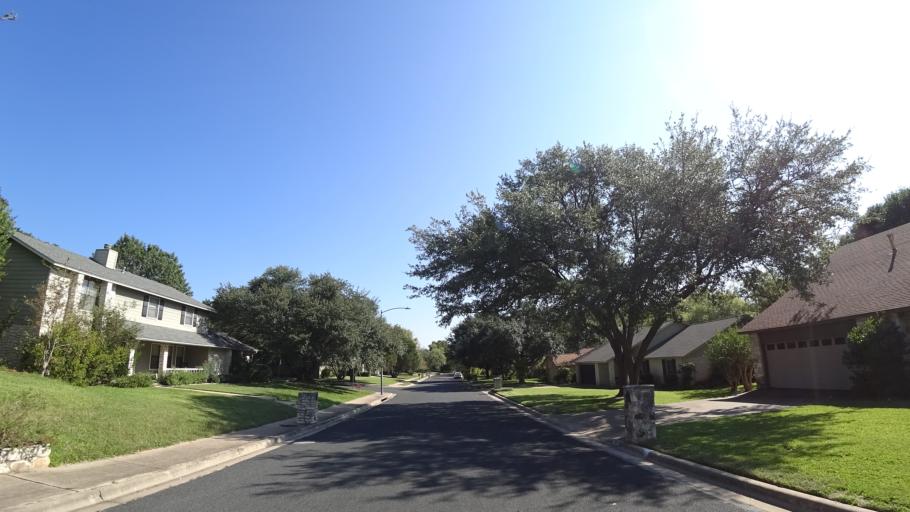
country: US
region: Texas
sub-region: Travis County
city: Rollingwood
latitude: 30.2686
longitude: -97.8109
